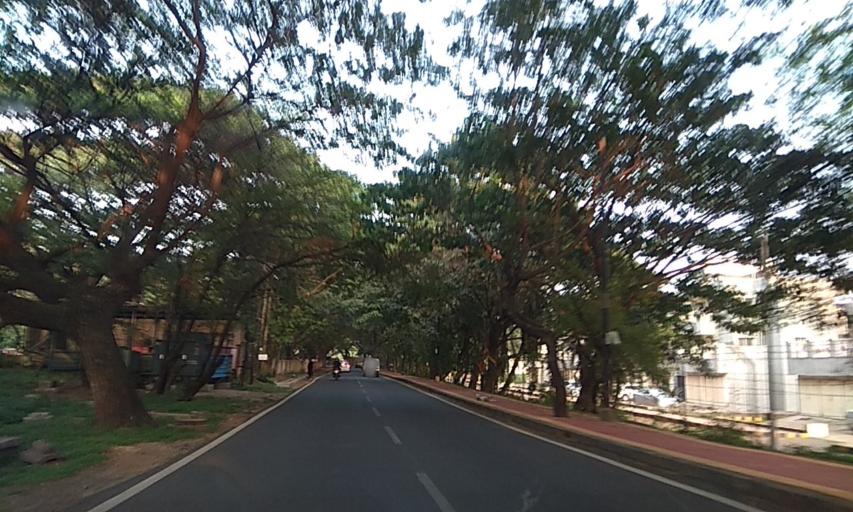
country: IN
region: Maharashtra
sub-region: Pune Division
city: Khadki
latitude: 18.5569
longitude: 73.8560
